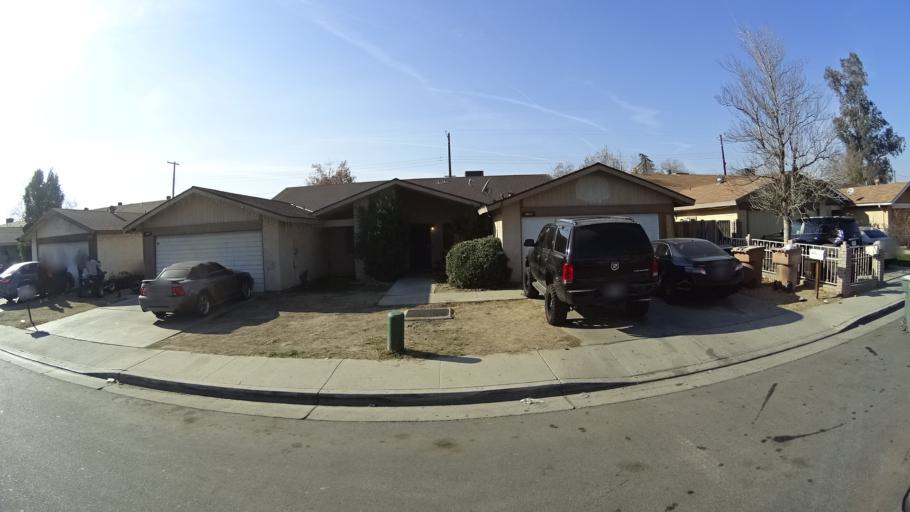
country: US
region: California
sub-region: Kern County
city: Bakersfield
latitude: 35.3259
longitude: -119.0116
